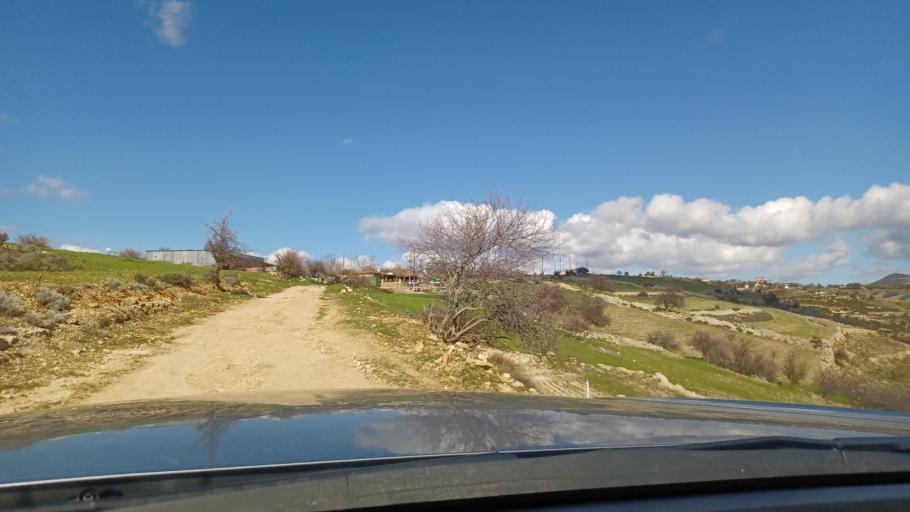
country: CY
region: Limassol
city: Pachna
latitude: 34.8204
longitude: 32.7915
